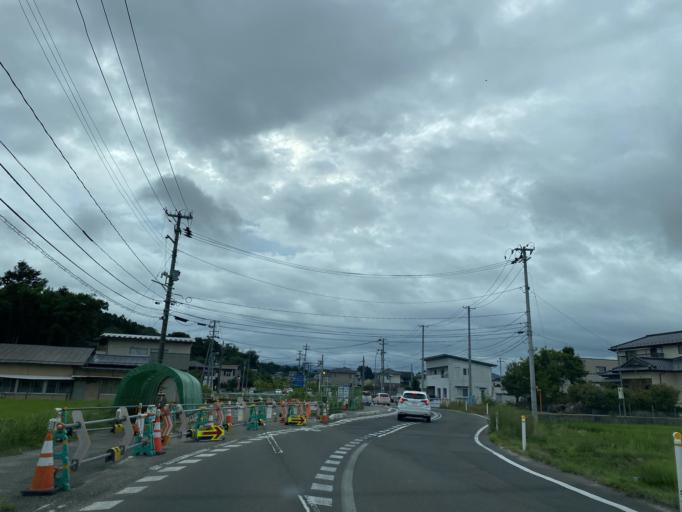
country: JP
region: Miyagi
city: Tomiya
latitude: 38.3953
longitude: 140.8984
